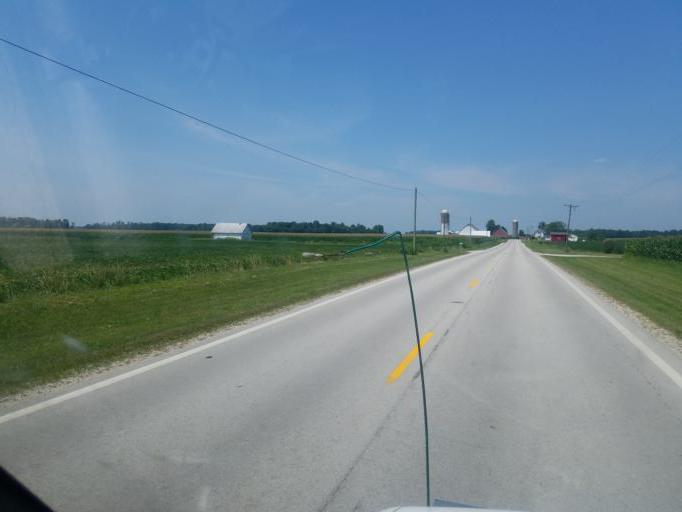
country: US
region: Ohio
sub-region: Shelby County
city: Fort Loramie
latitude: 40.3496
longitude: -84.4346
